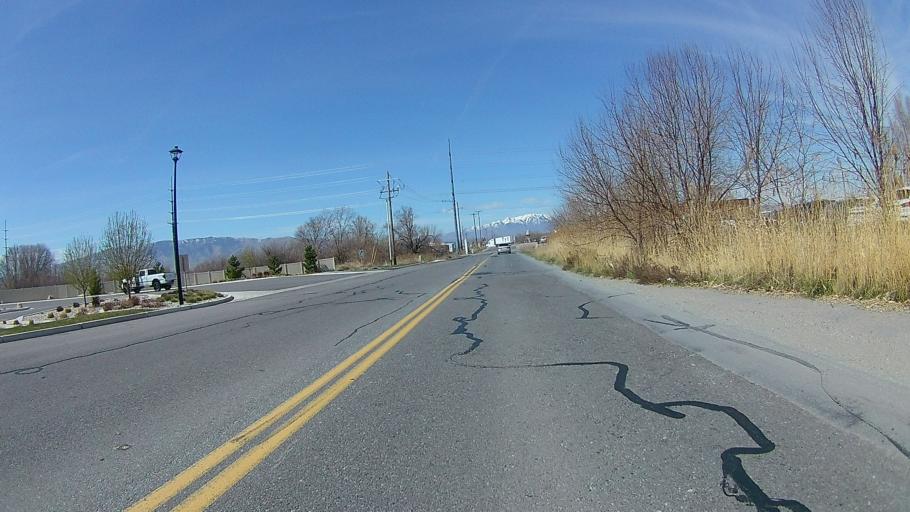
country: US
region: Utah
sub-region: Utah County
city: American Fork
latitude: 40.3551
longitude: -111.7843
